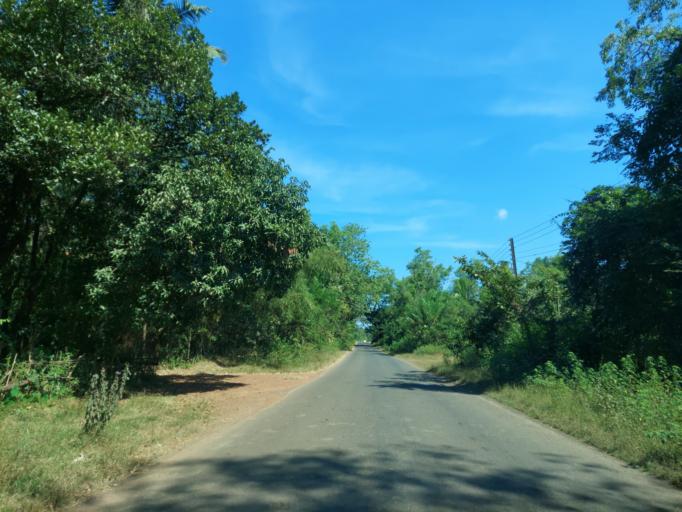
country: IN
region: Maharashtra
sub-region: Sindhudurg
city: Kudal
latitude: 15.9876
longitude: 73.6731
